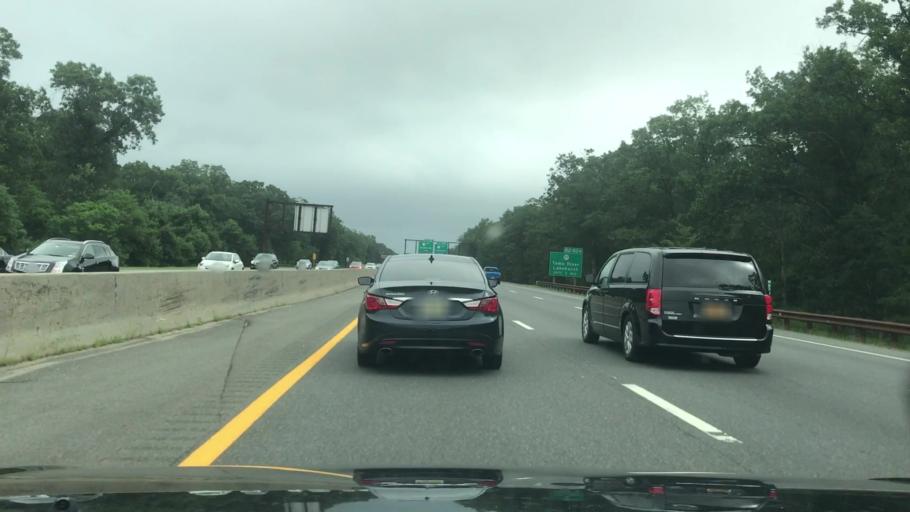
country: US
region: New Jersey
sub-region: Ocean County
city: Silver Ridge
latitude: 39.9791
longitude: -74.2128
